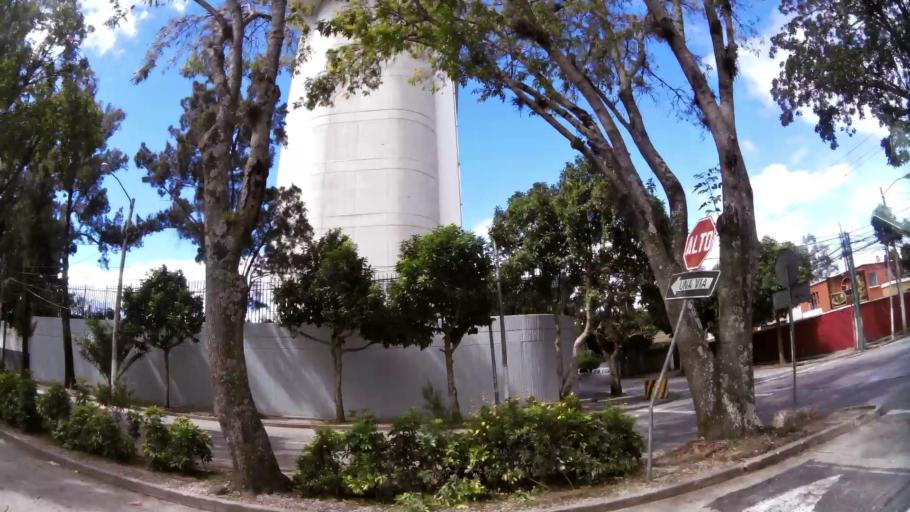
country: GT
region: Guatemala
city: Guatemala City
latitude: 14.6048
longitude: -90.5244
